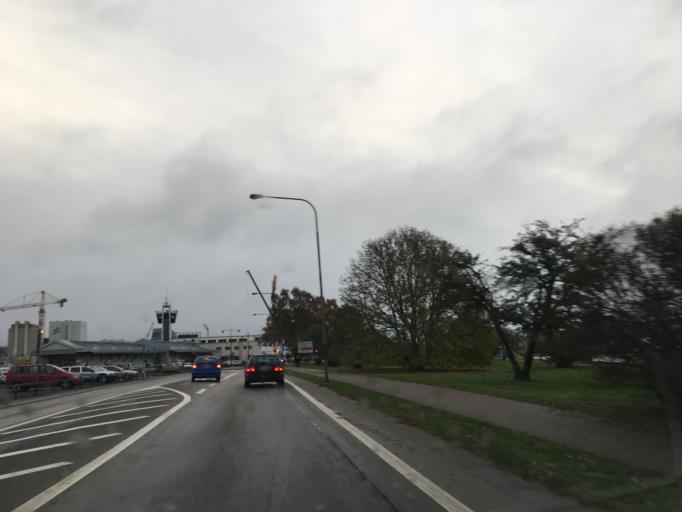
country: SE
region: Kalmar
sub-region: Kalmar Kommun
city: Kalmar
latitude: 56.6613
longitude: 16.3577
